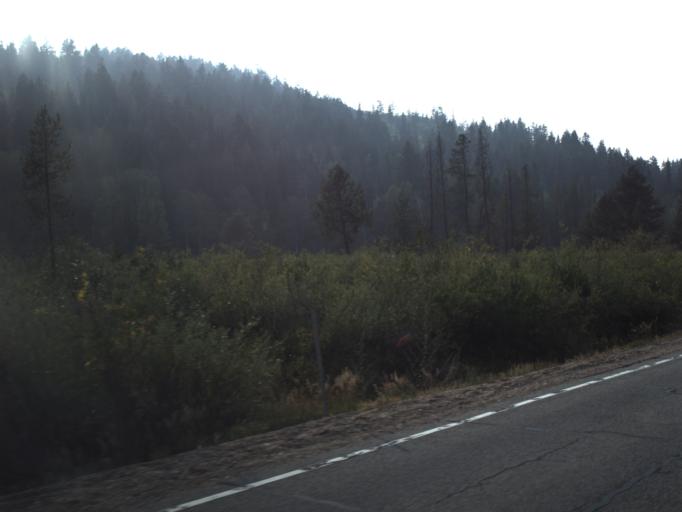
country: US
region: Utah
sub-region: Summit County
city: Francis
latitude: 40.6135
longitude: -111.1278
